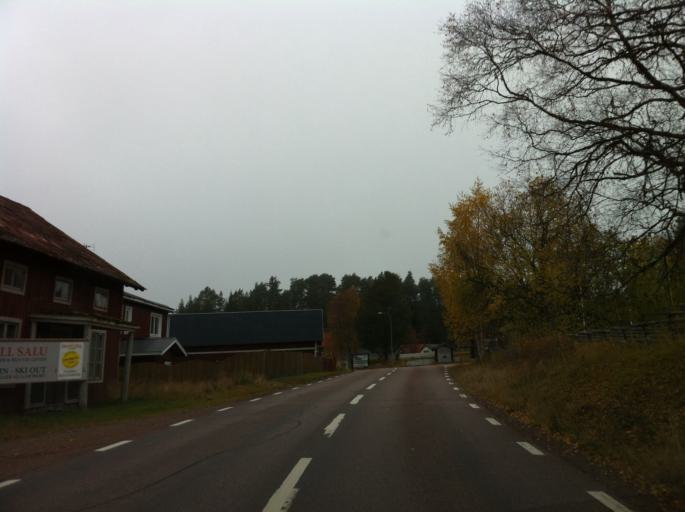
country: NO
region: Hedmark
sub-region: Trysil
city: Innbygda
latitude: 61.8560
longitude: 12.7328
